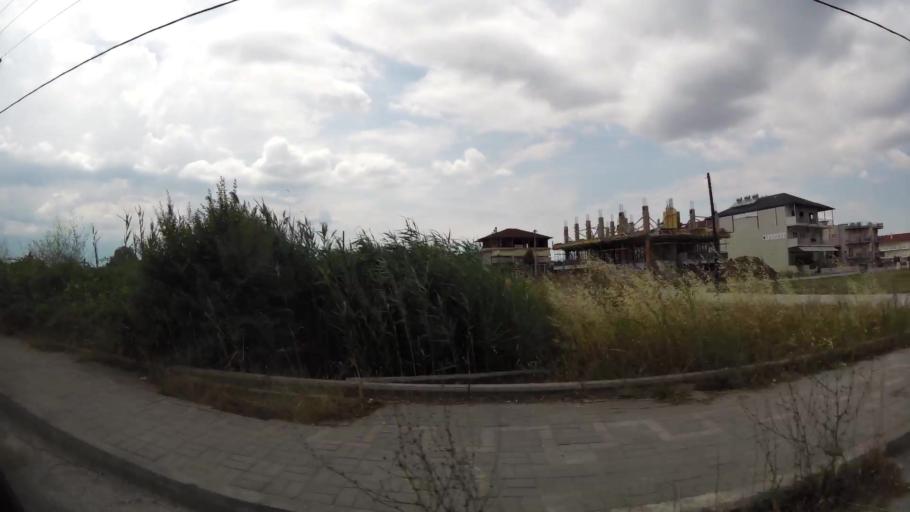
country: GR
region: Central Macedonia
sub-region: Nomos Pierias
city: Paralia
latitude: 40.2737
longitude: 22.5957
